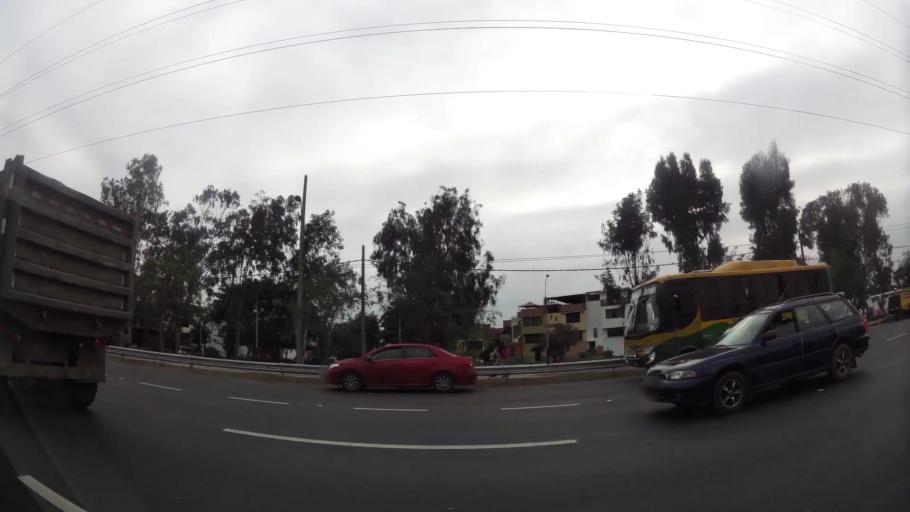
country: PE
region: Lima
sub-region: Lima
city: Surco
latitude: -12.1528
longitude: -76.9839
